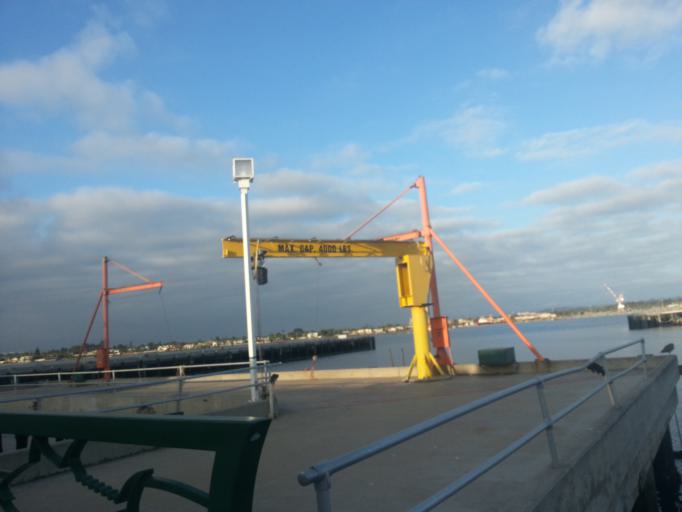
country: US
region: California
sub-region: San Diego County
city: San Diego
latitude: 32.7092
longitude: -117.1719
